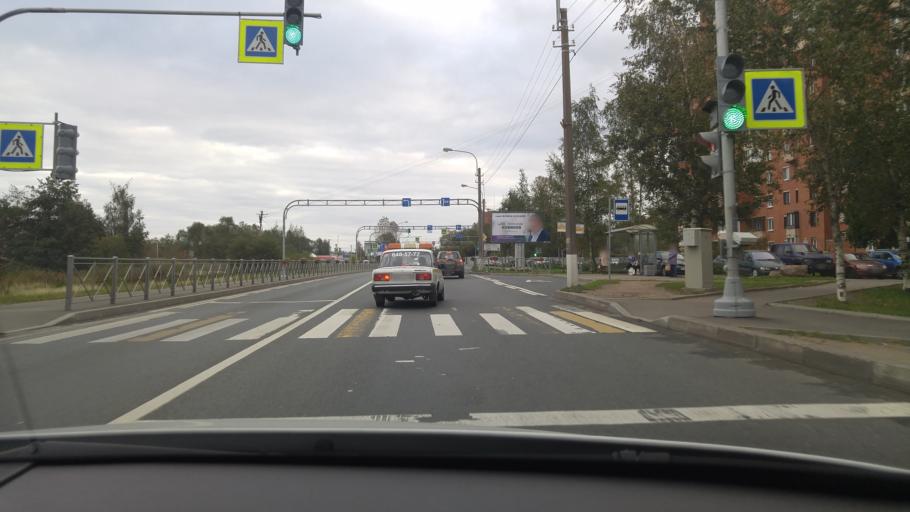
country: RU
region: St.-Petersburg
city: Kronshtadt
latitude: 60.0113
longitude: 29.7260
